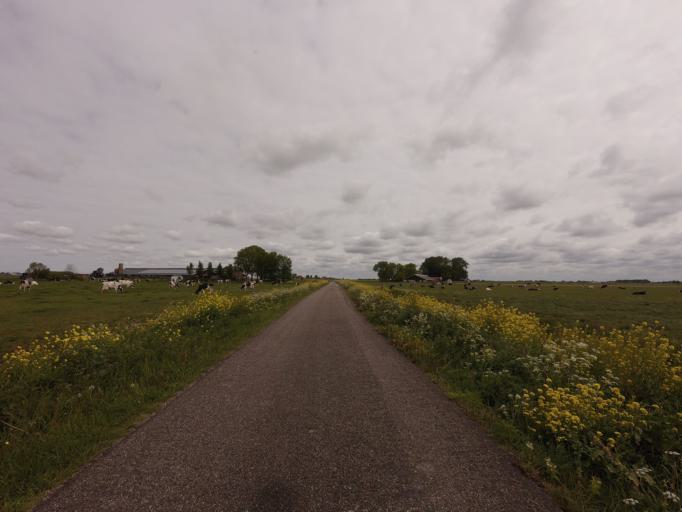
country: NL
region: Friesland
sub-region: Sudwest Fryslan
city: Workum
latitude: 52.9497
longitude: 5.4693
